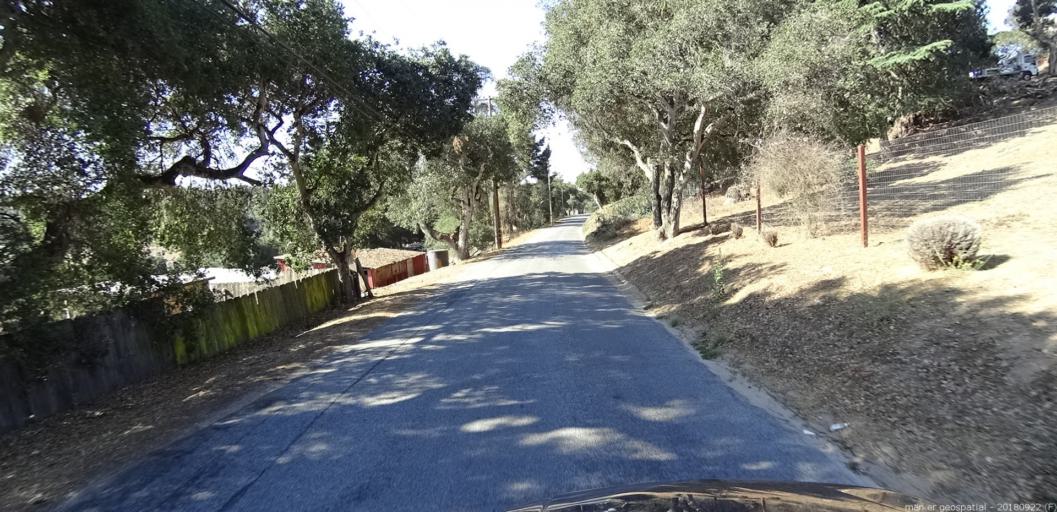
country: US
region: California
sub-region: Monterey County
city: Prunedale
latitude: 36.8134
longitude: -121.6433
